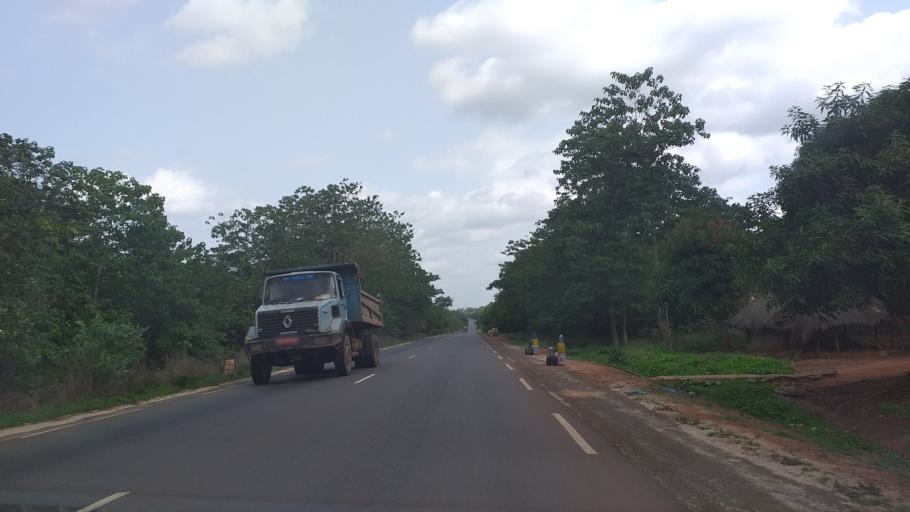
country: GN
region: Boke
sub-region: Boke Prefecture
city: Sangueya
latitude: 10.7427
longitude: -14.3793
